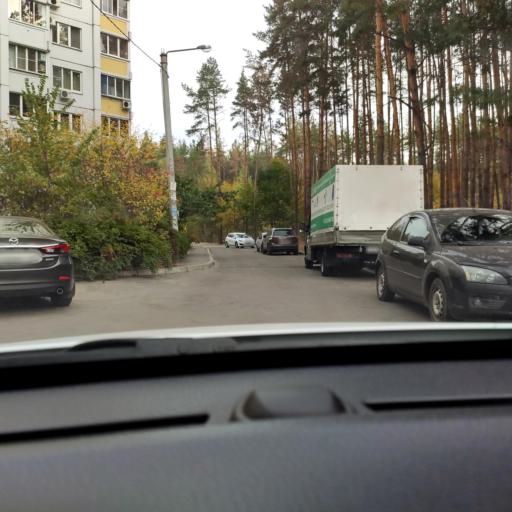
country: RU
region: Voronezj
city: Somovo
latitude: 51.6917
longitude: 39.2818
